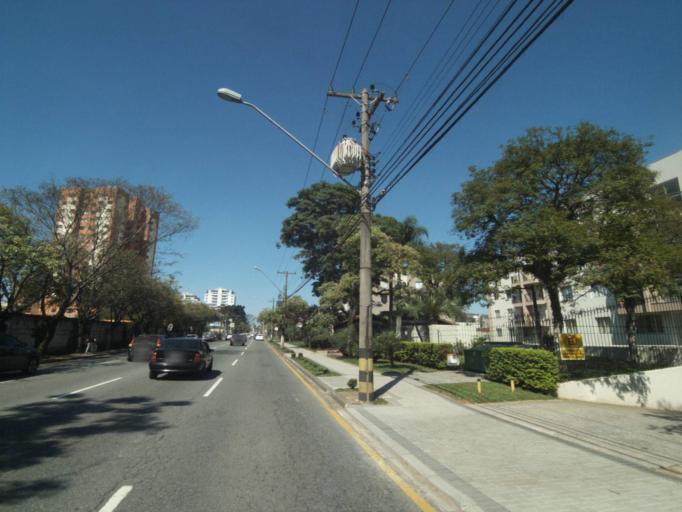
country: BR
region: Parana
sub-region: Curitiba
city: Curitiba
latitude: -25.3944
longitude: -49.2428
